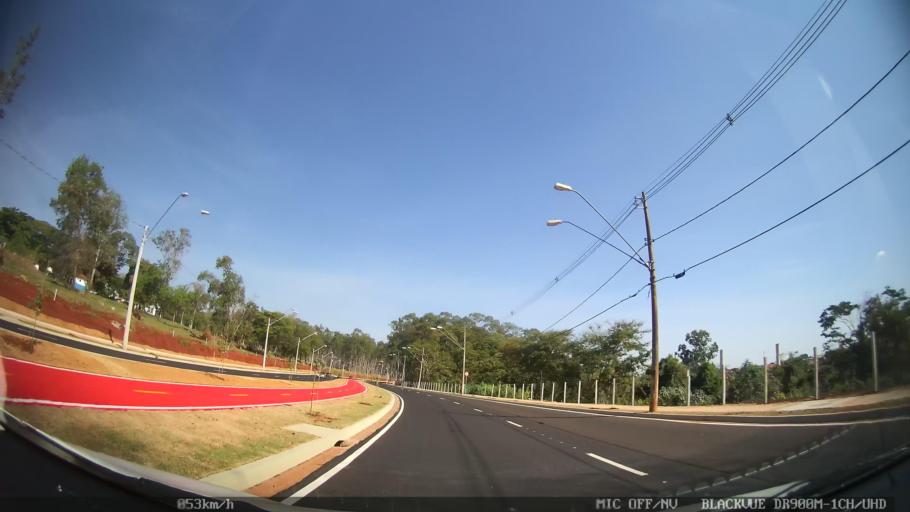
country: BR
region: Sao Paulo
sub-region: Ribeirao Preto
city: Ribeirao Preto
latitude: -21.2065
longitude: -47.8303
